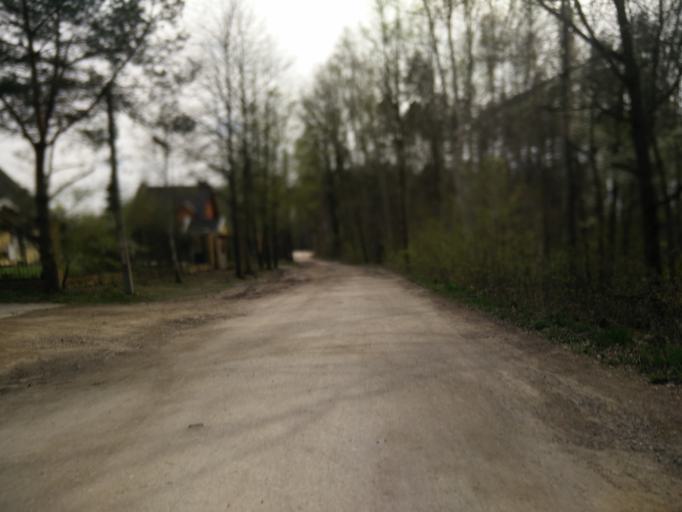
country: PL
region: Masovian Voivodeship
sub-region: Powiat warszawski zachodni
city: Izabelin
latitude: 52.2898
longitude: 20.8391
